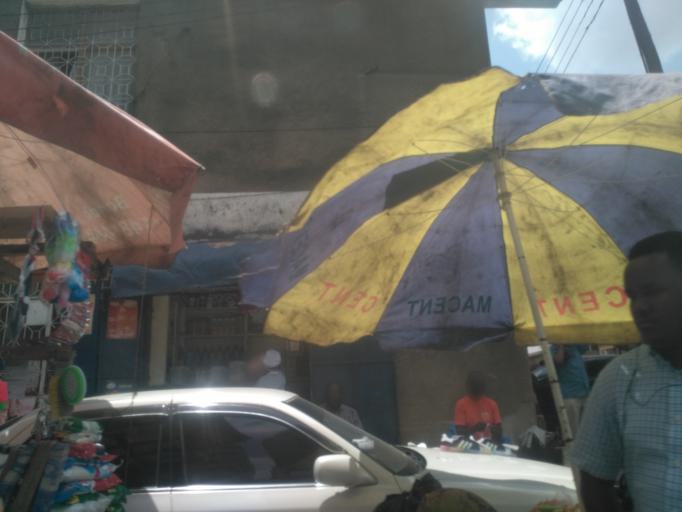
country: TZ
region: Dar es Salaam
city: Dar es Salaam
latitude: -6.8254
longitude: 39.2751
